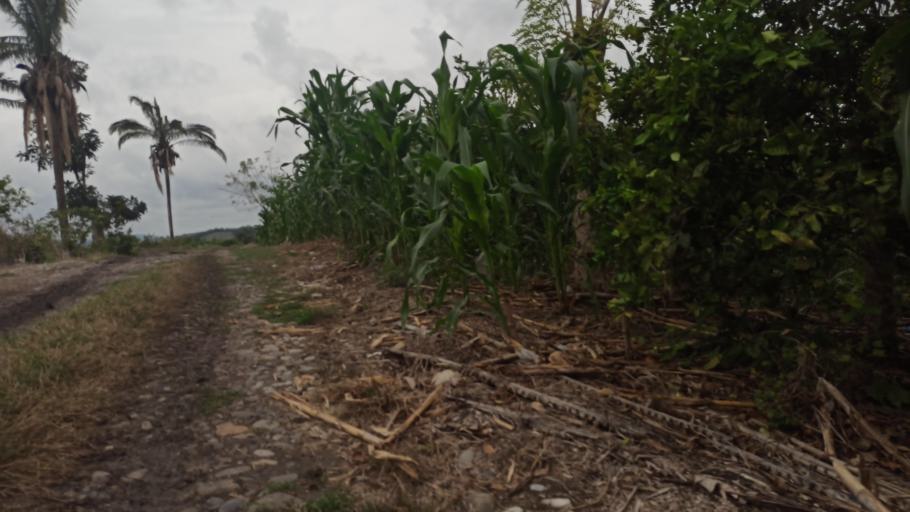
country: MX
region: Puebla
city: Espinal
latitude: 20.3003
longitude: -97.4078
